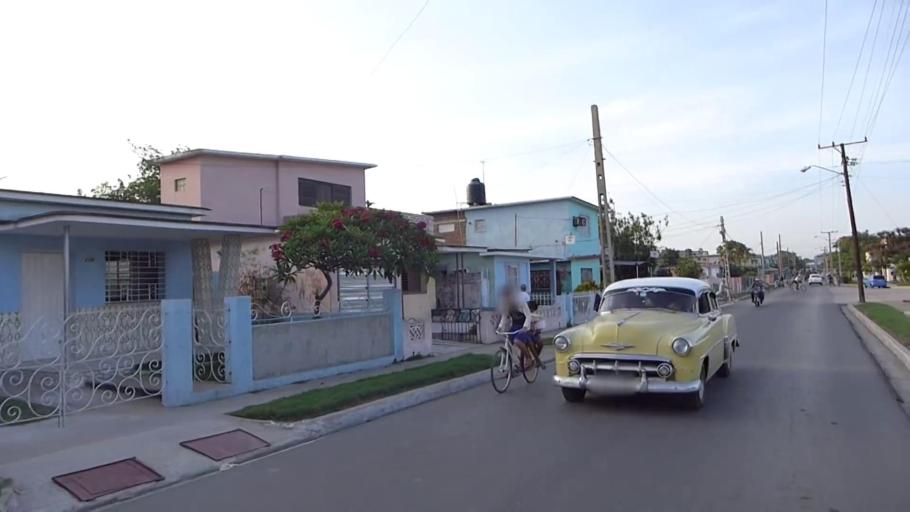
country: CU
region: Camaguey
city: Camaguey
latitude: 21.3818
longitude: -77.9365
